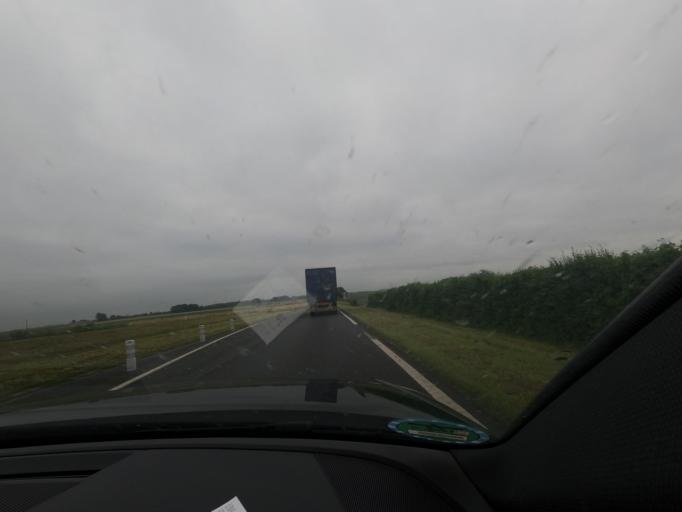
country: FR
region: Picardie
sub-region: Departement de la Somme
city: Harbonnieres
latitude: 49.7797
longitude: 2.5952
